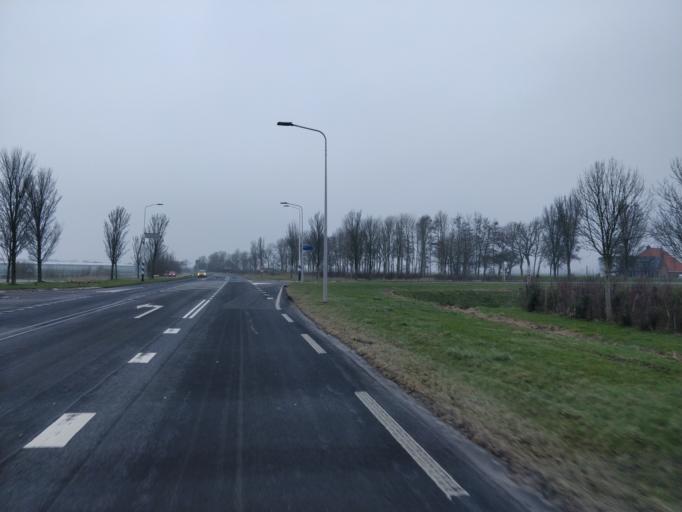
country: NL
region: Friesland
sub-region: Menameradiel
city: Menaam
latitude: 53.2378
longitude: 5.6792
